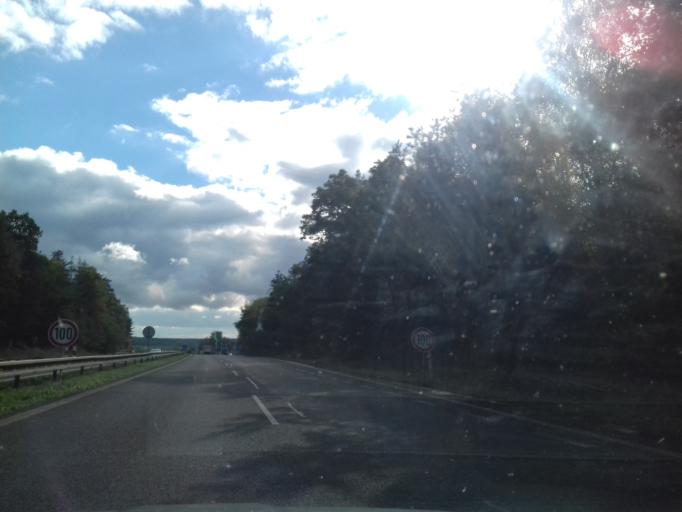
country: CZ
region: Central Bohemia
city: Lustenice
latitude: 50.3467
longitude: 14.8715
